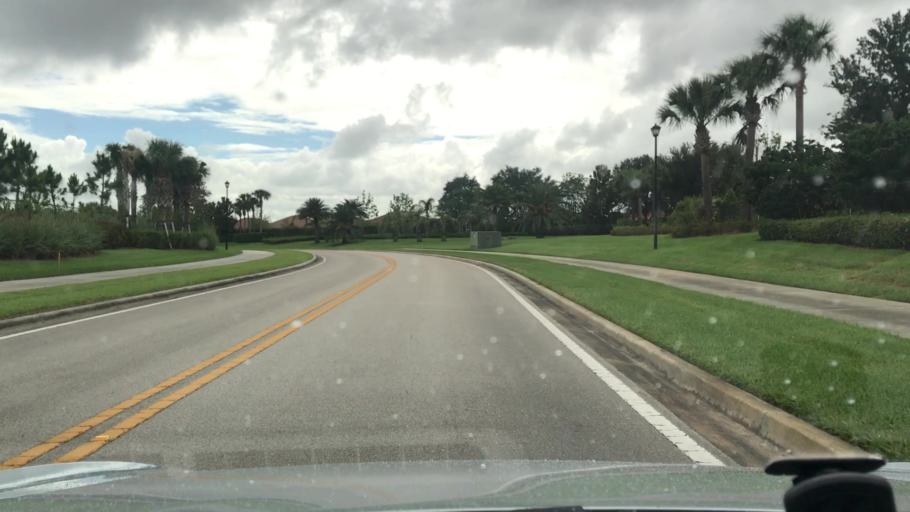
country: US
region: Florida
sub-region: Indian River County
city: Gifford
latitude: 27.6863
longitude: -80.4373
